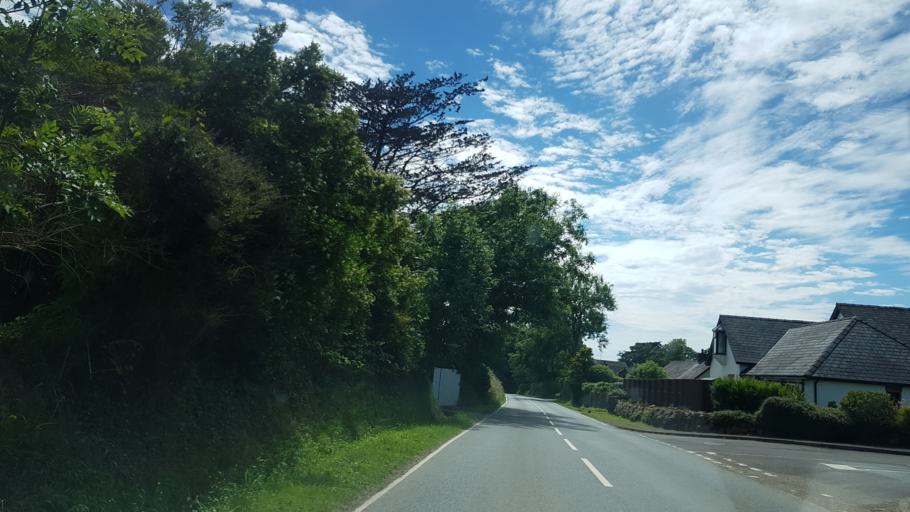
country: GB
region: Wales
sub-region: Pembrokeshire
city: Haverfordwest
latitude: 51.8234
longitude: -4.9481
